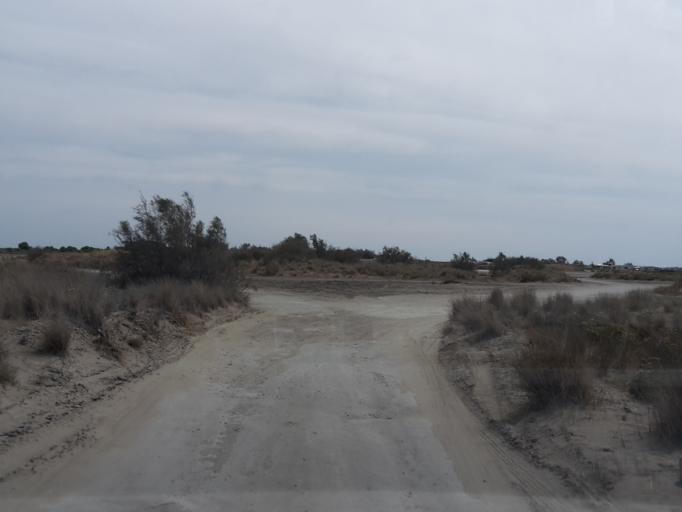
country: FR
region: Provence-Alpes-Cote d'Azur
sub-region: Departement des Bouches-du-Rhone
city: Saintes-Maries-de-la-Mer
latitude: 43.4063
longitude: 4.5968
